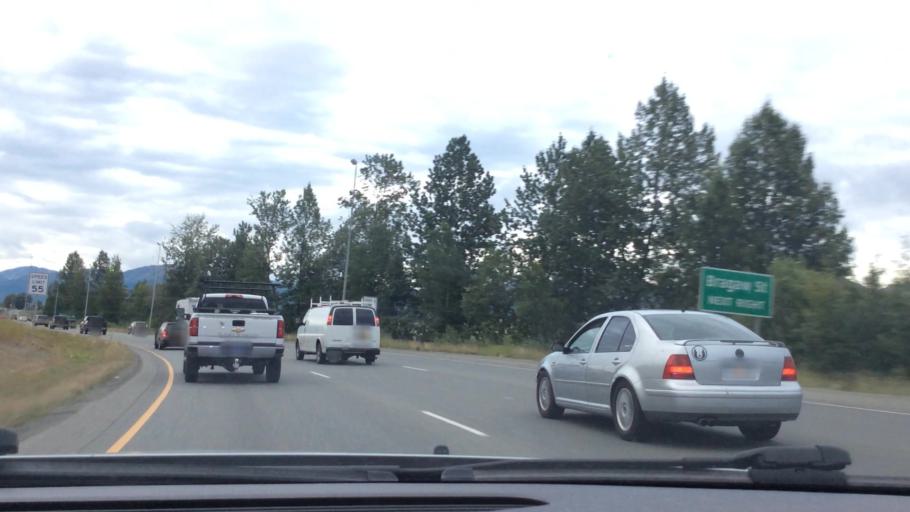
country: US
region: Alaska
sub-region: Anchorage Municipality
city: Anchorage
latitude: 61.2176
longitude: -149.8231
